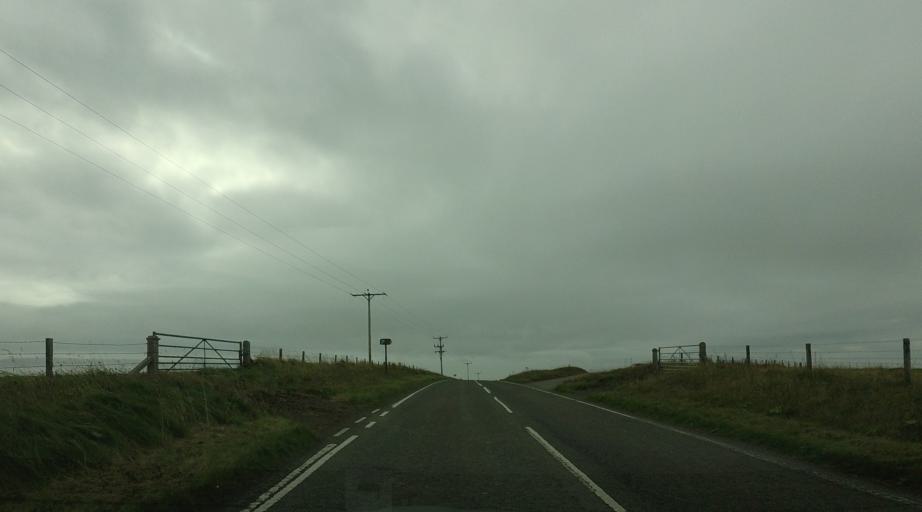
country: GB
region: Scotland
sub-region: Orkney Islands
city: Orkney
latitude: 58.7754
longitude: -2.9605
